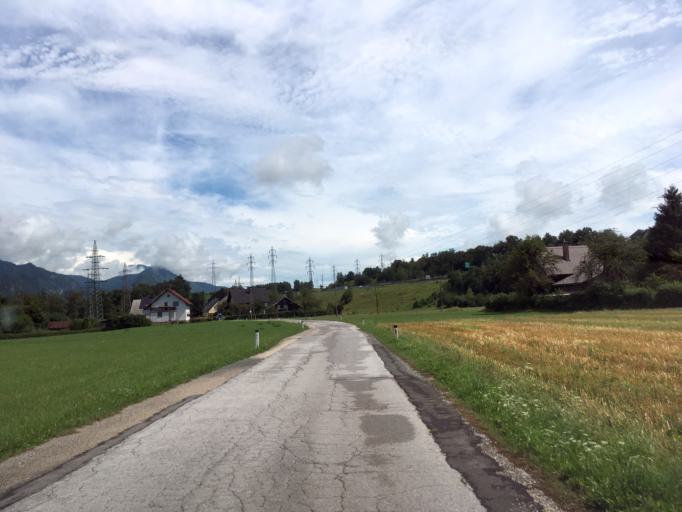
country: SI
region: Jesenice
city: Slovenski Javornik
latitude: 46.4160
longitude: 14.0972
